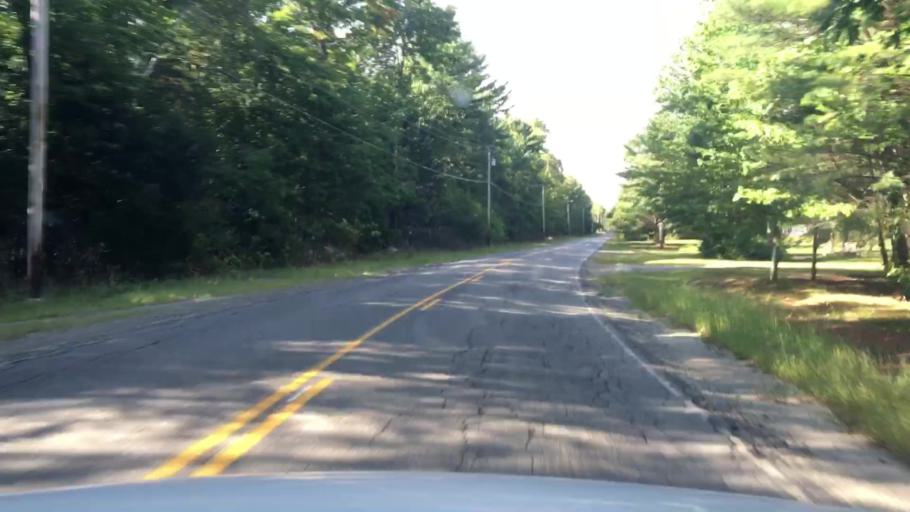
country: US
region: Maine
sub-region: Penobscot County
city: Enfield
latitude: 45.2186
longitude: -68.5352
